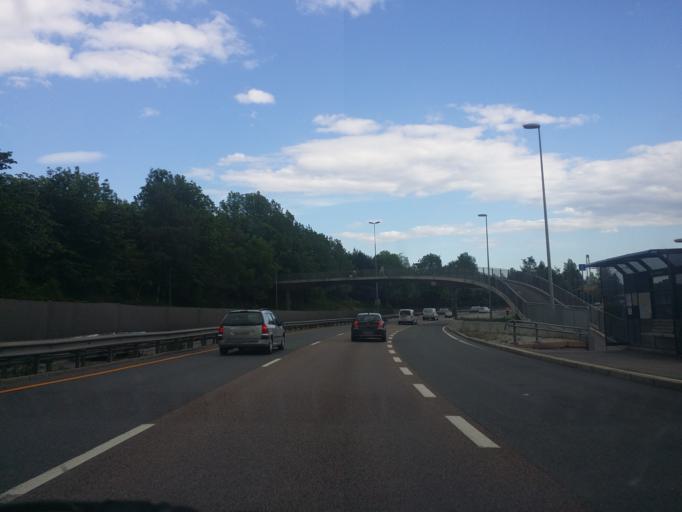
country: NO
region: Oslo
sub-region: Oslo
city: Oslo
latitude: 59.9512
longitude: 10.7756
